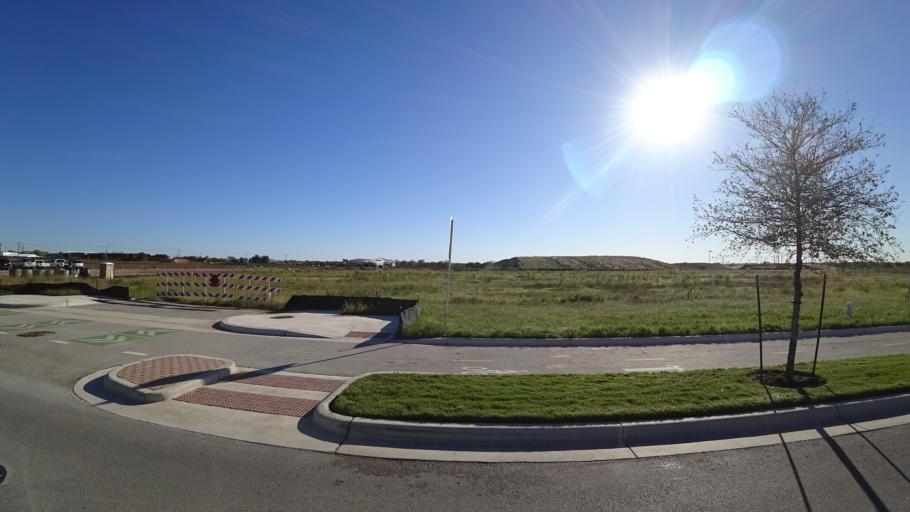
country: US
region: Texas
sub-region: Travis County
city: Austin
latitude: 30.2936
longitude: -97.6951
